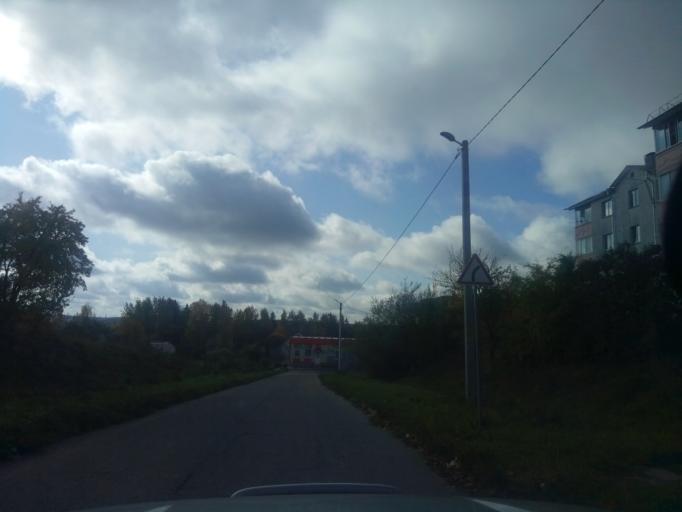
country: BY
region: Minsk
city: Zaslawye
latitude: 54.0104
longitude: 27.3080
